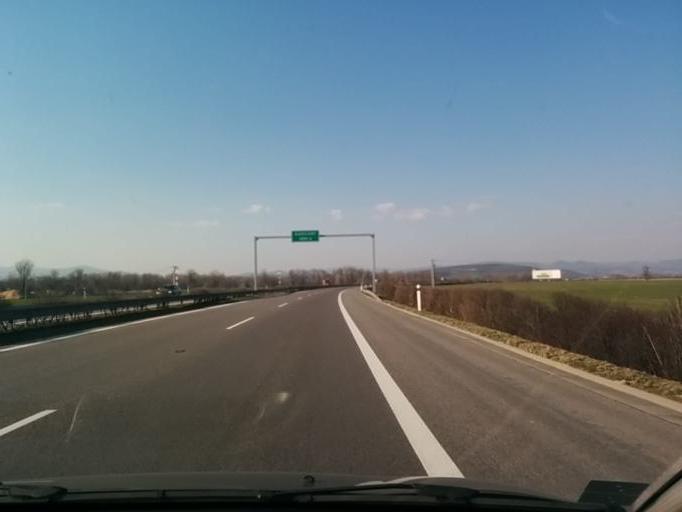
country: SK
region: Trenciansky
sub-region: Okres Nove Mesto nad Vahom
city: Nove Mesto nad Vahom
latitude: 48.7396
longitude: 17.8617
